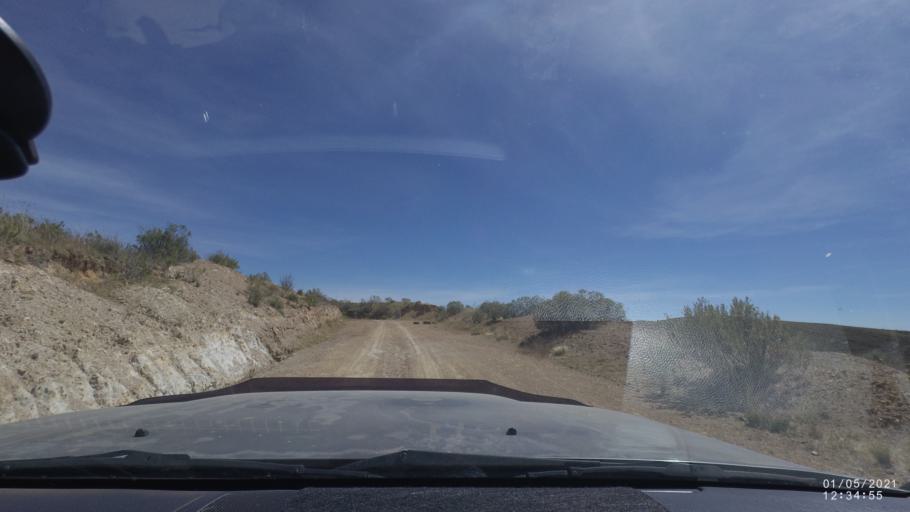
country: BO
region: Cochabamba
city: Capinota
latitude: -17.6770
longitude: -66.1542
